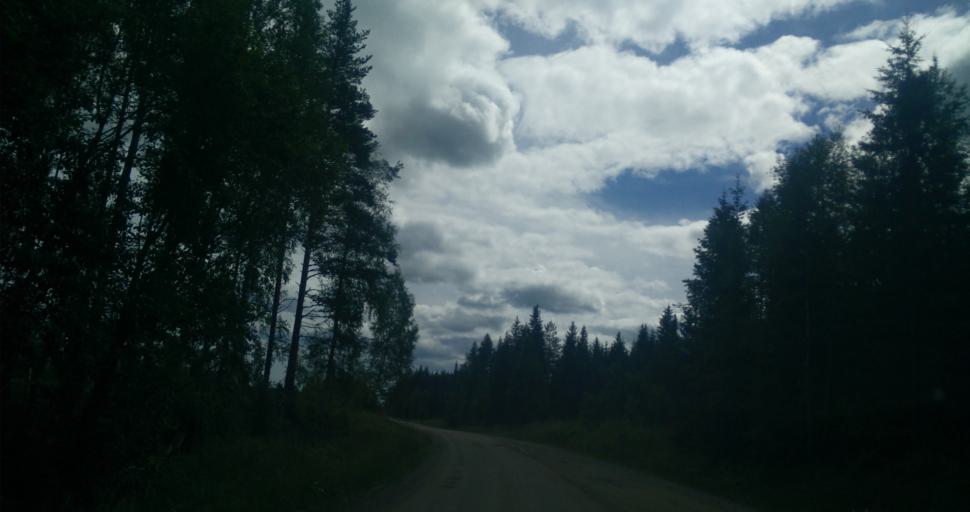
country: SE
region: Gaevleborg
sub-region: Nordanstigs Kommun
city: Bergsjoe
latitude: 62.1088
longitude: 17.0996
